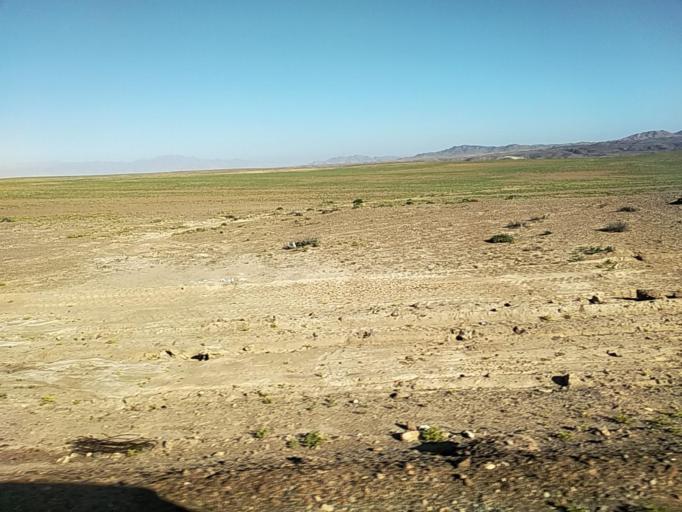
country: CL
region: Atacama
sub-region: Provincia de Copiapo
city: Copiapo
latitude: -27.3271
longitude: -70.7639
